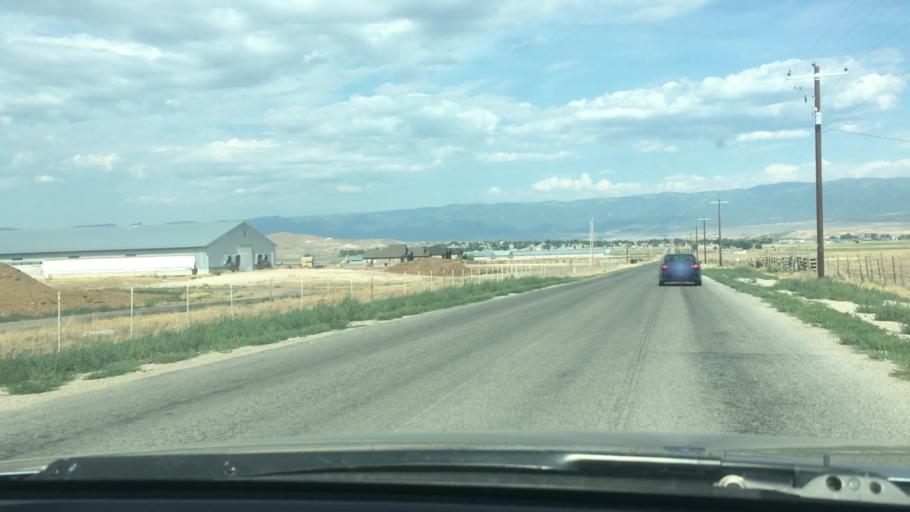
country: US
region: Utah
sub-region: Sanpete County
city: Moroni
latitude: 39.5235
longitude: -111.6276
